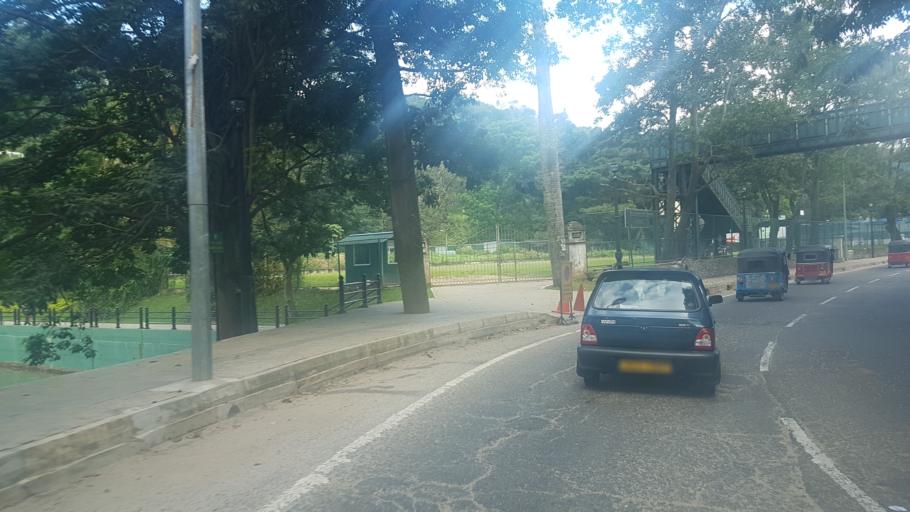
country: LK
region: Central
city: Kandy
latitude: 7.2879
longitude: 80.6453
